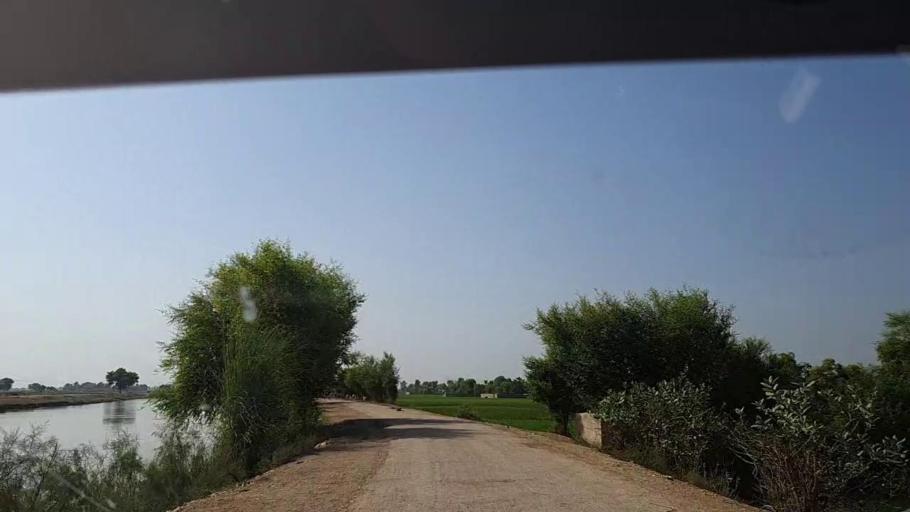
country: PK
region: Sindh
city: Ghauspur
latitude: 28.1922
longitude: 69.0555
